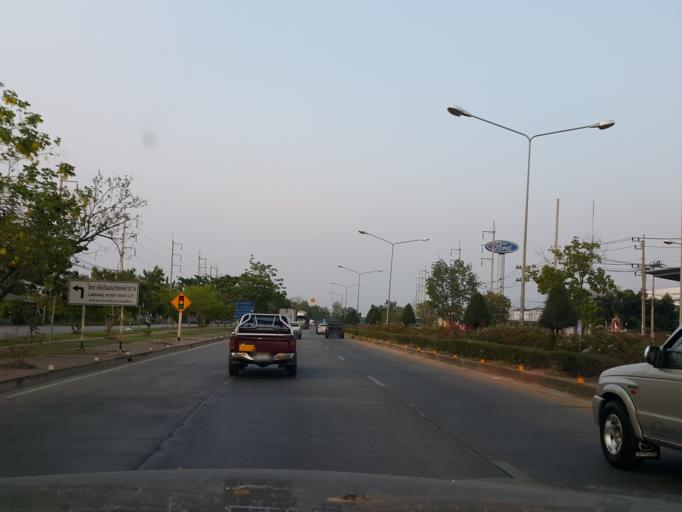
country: TH
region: Lampang
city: Lampang
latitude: 18.2511
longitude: 99.4530
